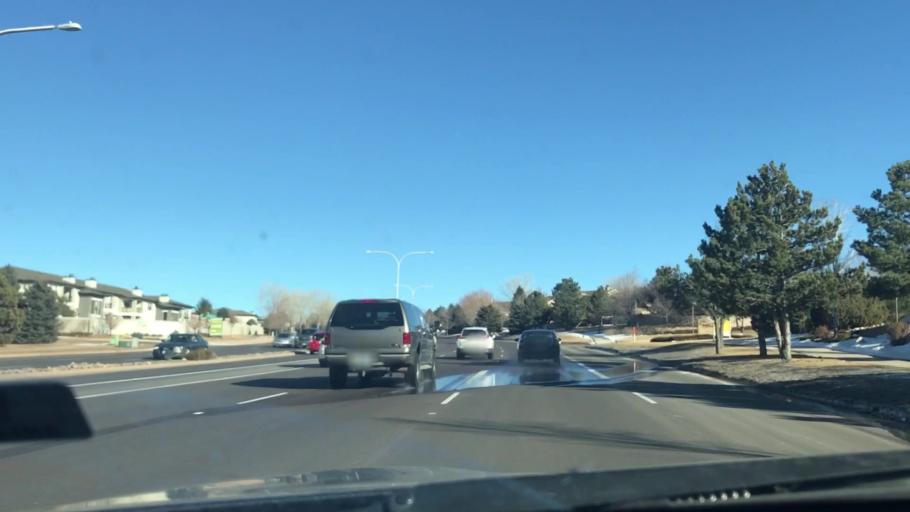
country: US
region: Colorado
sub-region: El Paso County
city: Air Force Academy
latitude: 38.9666
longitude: -104.7830
